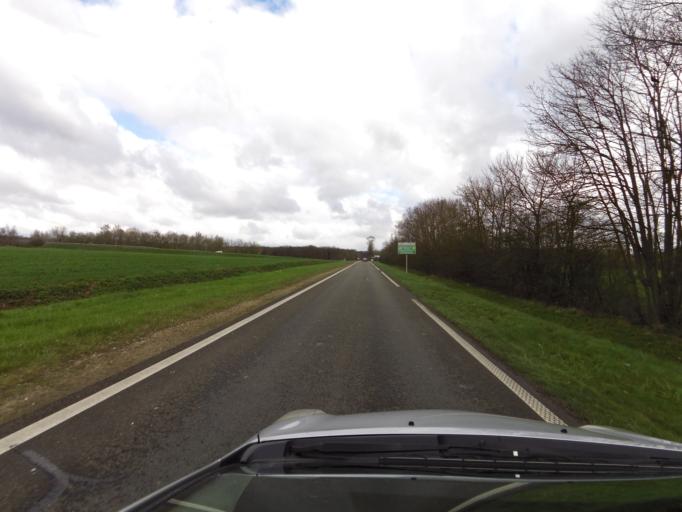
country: FR
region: Picardie
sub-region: Departement de l'Oise
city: Chamant
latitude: 49.2240
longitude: 2.5912
